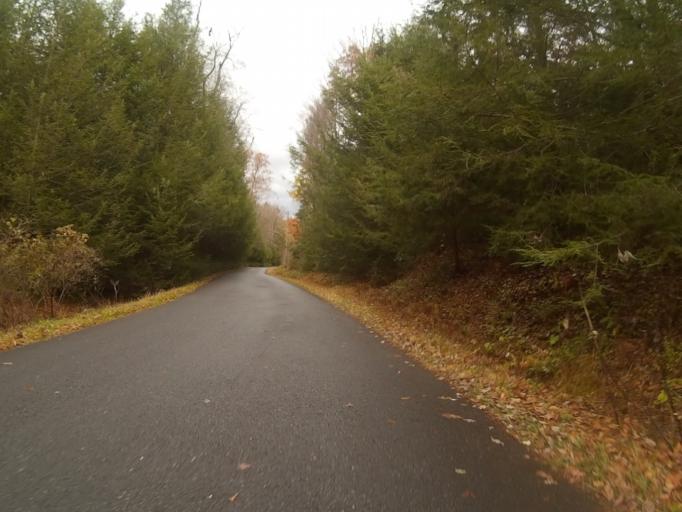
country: US
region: Pennsylvania
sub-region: Centre County
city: Boalsburg
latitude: 40.7567
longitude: -77.7348
